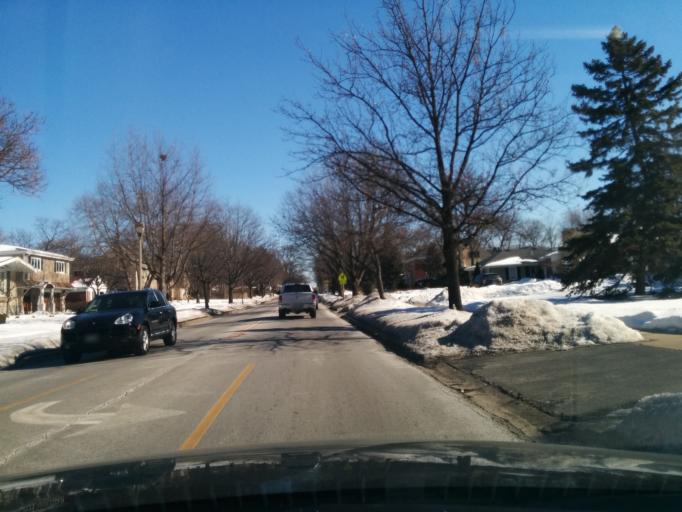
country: US
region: Illinois
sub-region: DuPage County
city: Elmhurst
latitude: 41.8904
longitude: -87.9451
